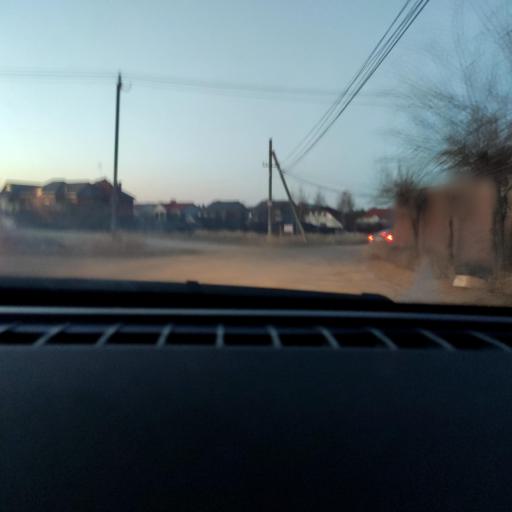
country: RU
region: Voronezj
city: Podgornoye
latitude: 51.7443
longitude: 39.1615
